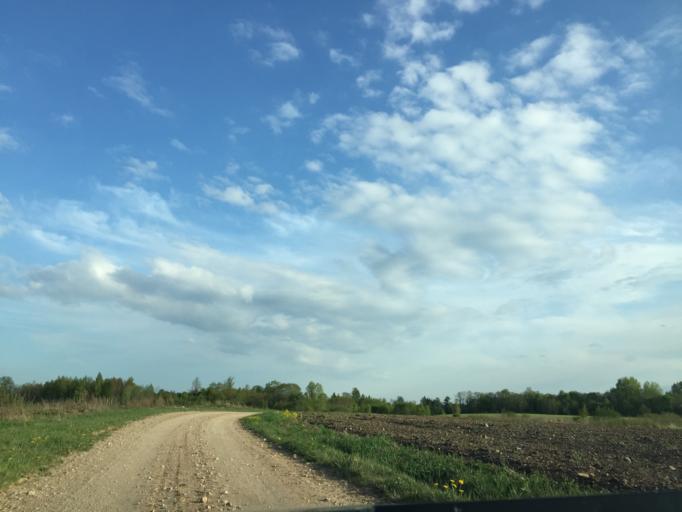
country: LV
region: Limbazu Rajons
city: Limbazi
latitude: 57.3762
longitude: 24.6383
